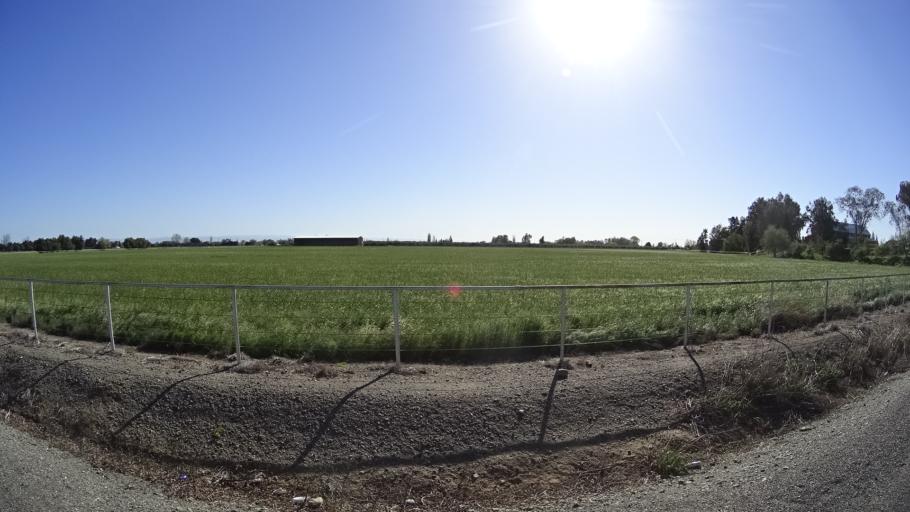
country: US
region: California
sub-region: Glenn County
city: Orland
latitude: 39.7611
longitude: -122.2479
